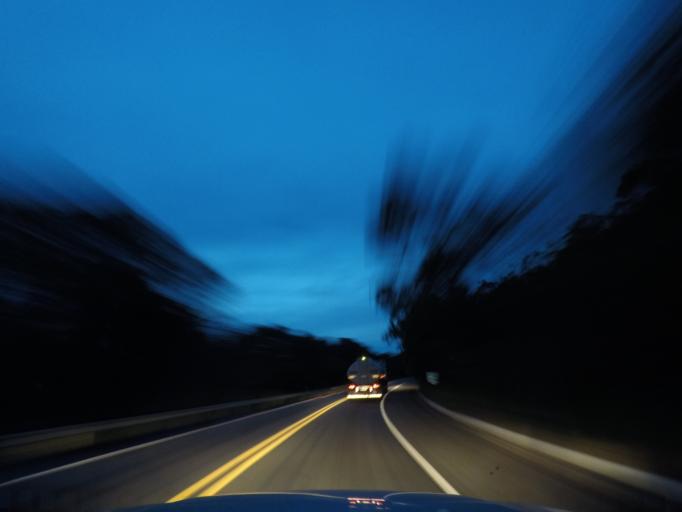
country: BR
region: Bahia
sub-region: Andarai
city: Vera Cruz
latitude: -12.4986
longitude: -41.3317
